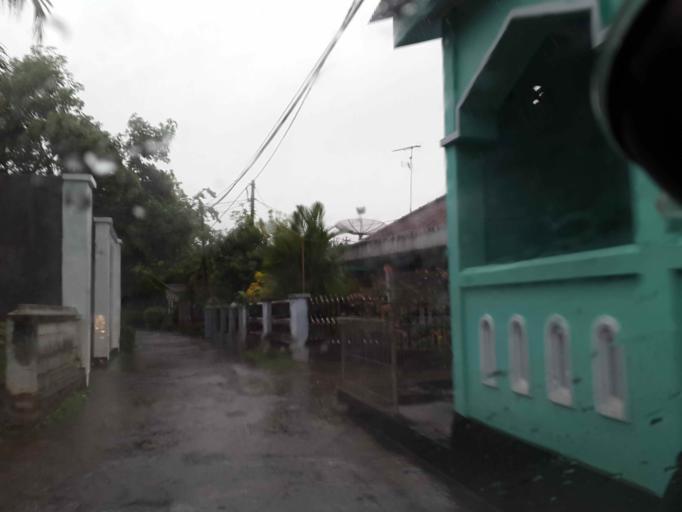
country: ID
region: Central Java
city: Kutoarjo
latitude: -7.7173
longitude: 110.0036
